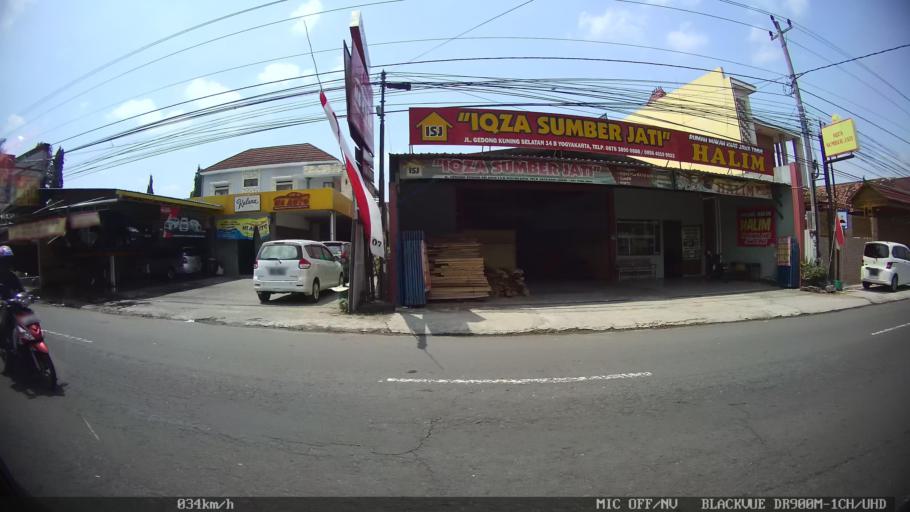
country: ID
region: Daerah Istimewa Yogyakarta
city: Yogyakarta
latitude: -7.8180
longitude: 110.4018
